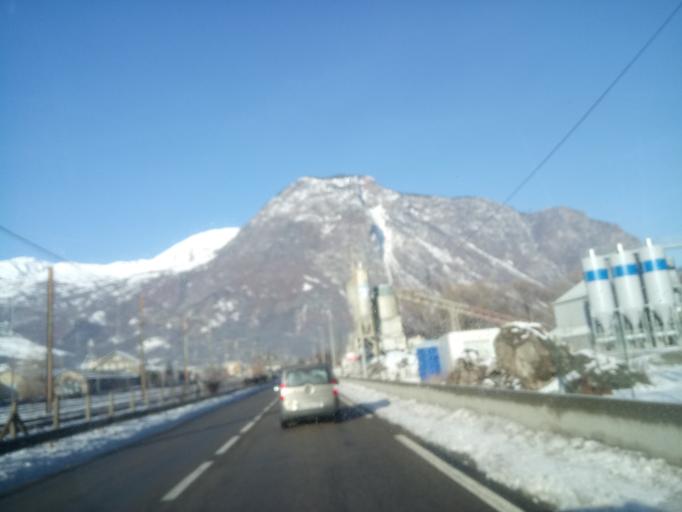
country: FR
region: Rhone-Alpes
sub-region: Departement de la Savoie
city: Villargondran
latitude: 45.2749
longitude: 6.3610
